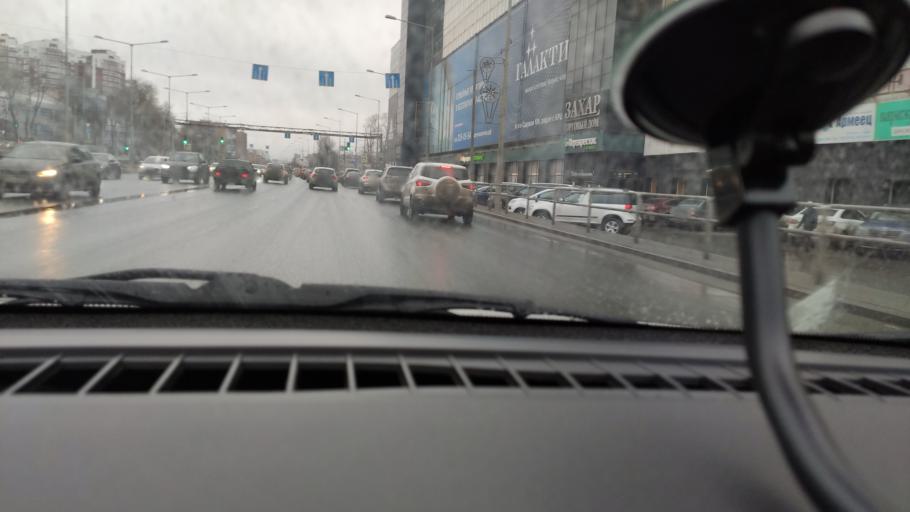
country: RU
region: Samara
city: Samara
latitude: 53.2178
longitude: 50.1480
